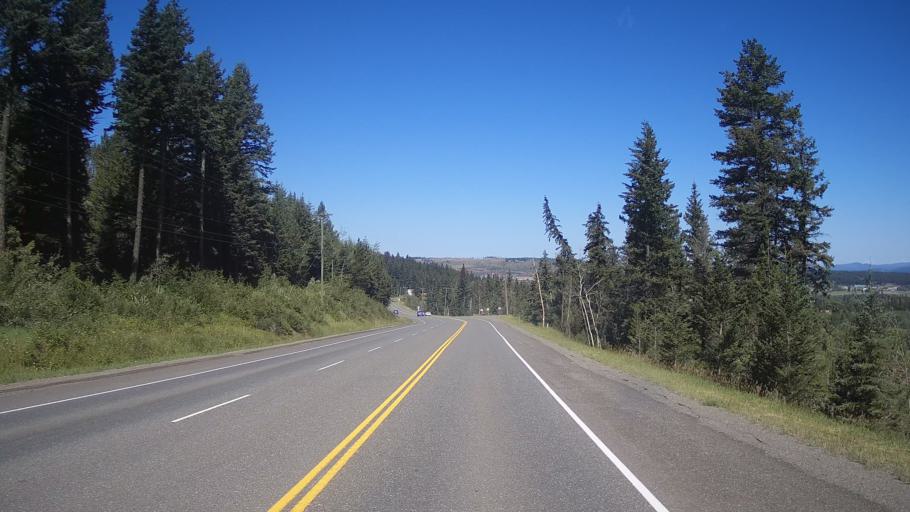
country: CA
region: British Columbia
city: Cache Creek
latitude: 51.6214
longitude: -121.2930
